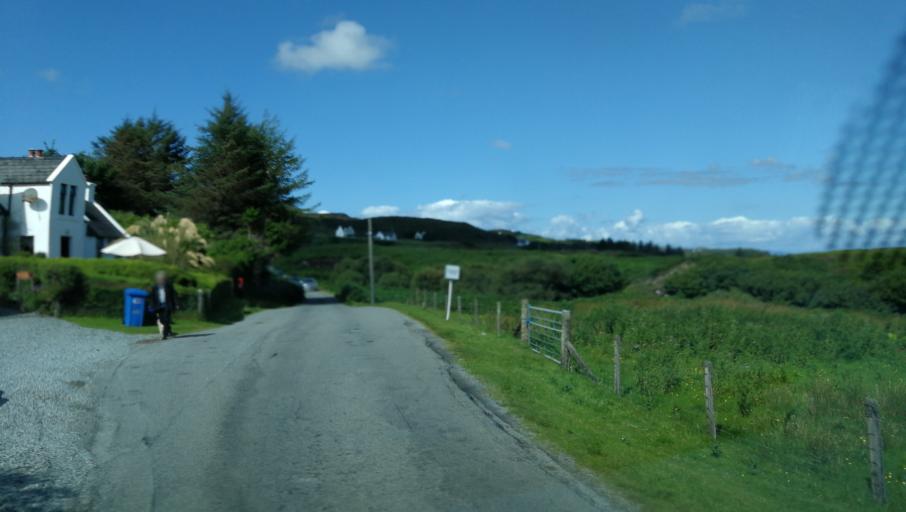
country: GB
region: Scotland
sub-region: Highland
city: Isle of Skye
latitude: 57.4380
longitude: -6.6333
